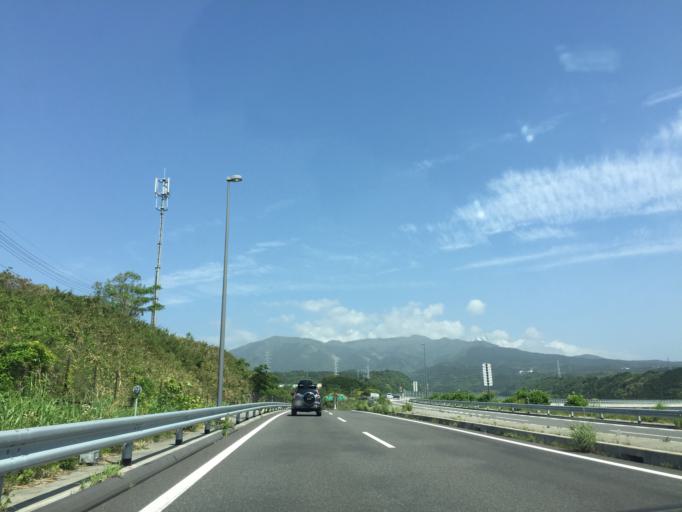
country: JP
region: Shizuoka
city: Numazu
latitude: 35.1537
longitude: 138.8700
